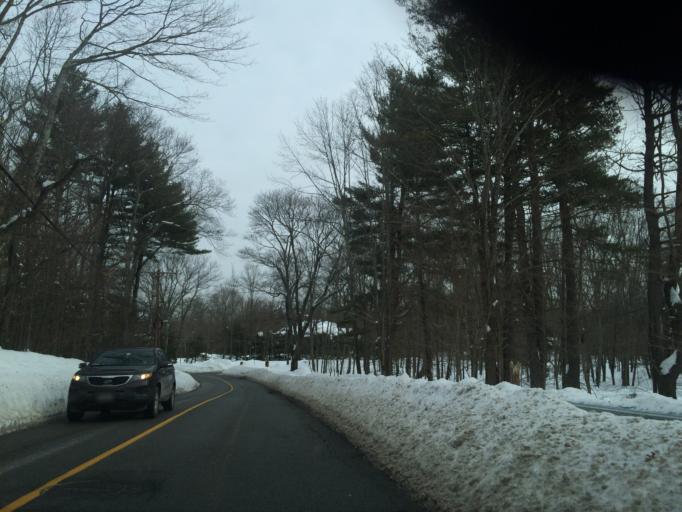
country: US
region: Massachusetts
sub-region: Middlesex County
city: Weston
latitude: 42.3611
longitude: -71.3152
